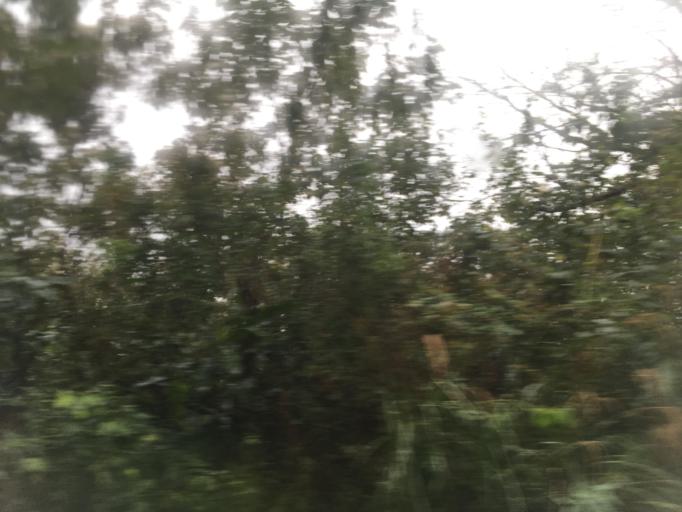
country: TW
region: Taiwan
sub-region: Keelung
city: Keelung
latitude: 25.0681
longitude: 121.9040
